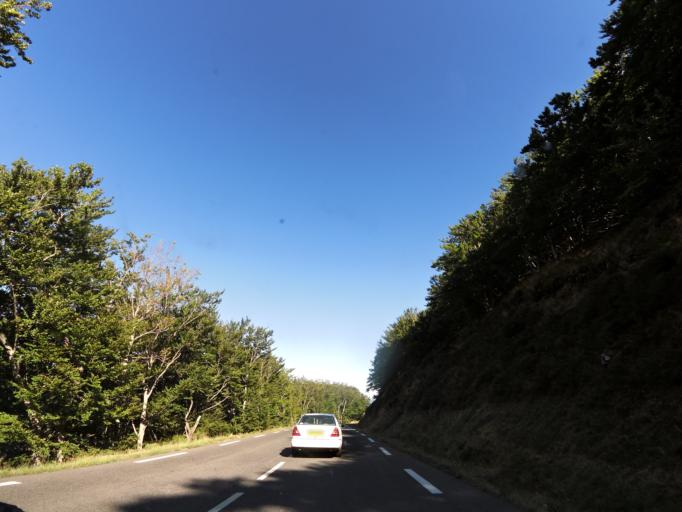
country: FR
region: Languedoc-Roussillon
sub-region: Departement du Gard
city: Valleraugue
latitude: 44.0883
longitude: 3.5744
